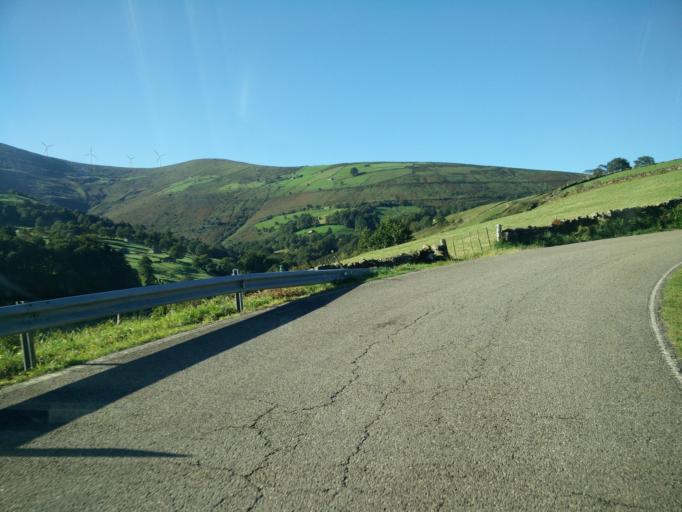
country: ES
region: Cantabria
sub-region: Provincia de Cantabria
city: San Pedro del Romeral
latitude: 43.1086
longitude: -3.8042
